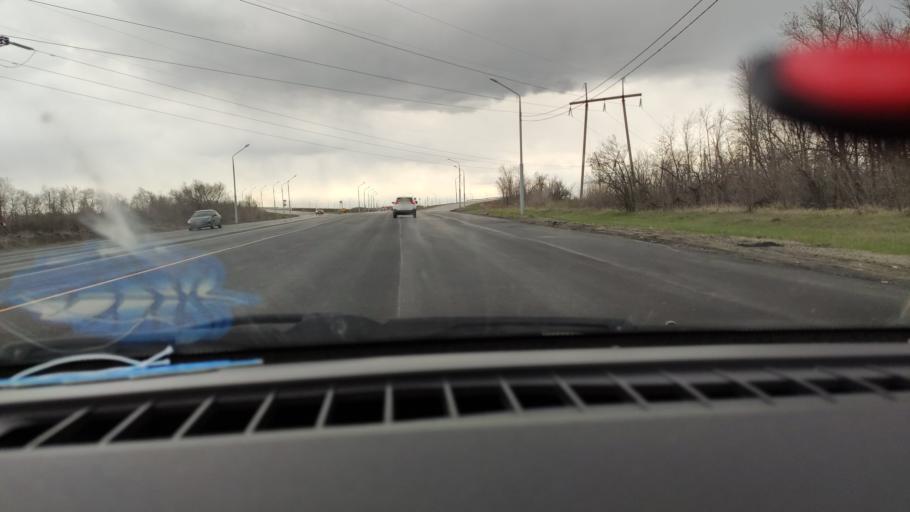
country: RU
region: Saratov
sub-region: Saratovskiy Rayon
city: Saratov
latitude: 51.6698
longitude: 45.9986
